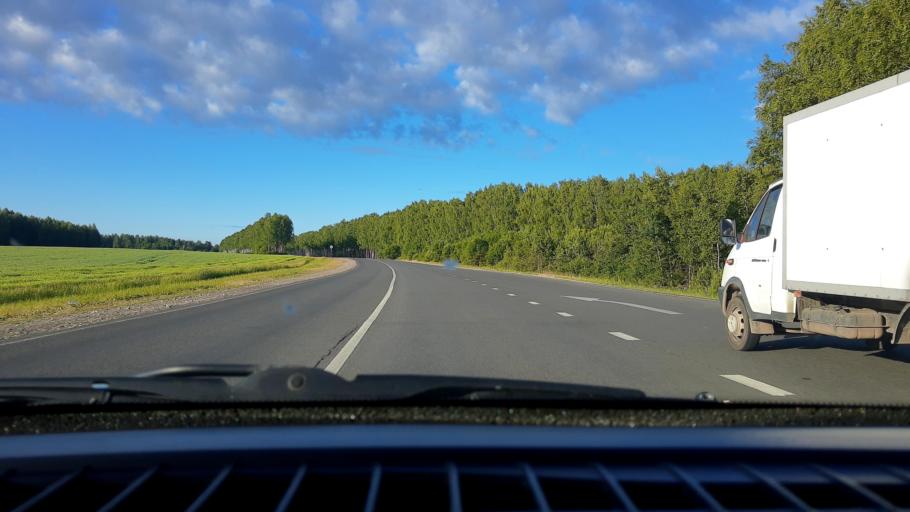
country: RU
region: Nizjnij Novgorod
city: Linda
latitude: 56.5792
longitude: 44.0230
